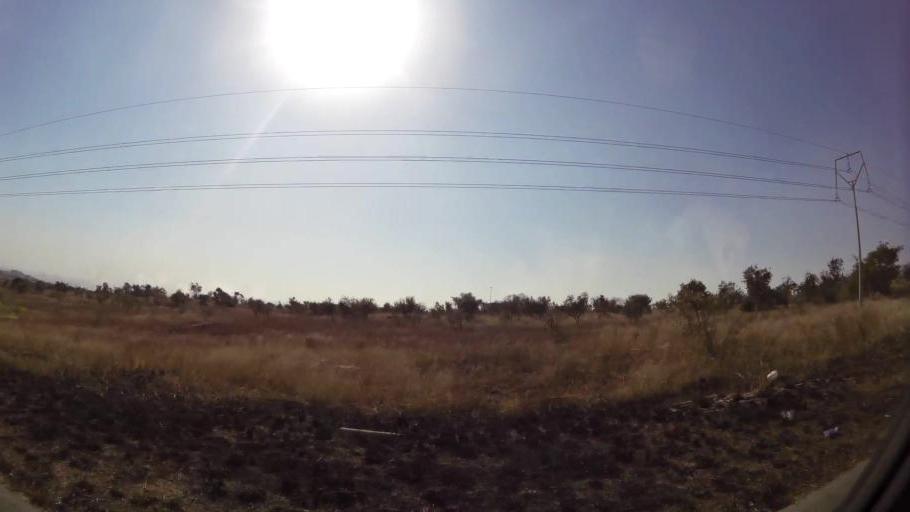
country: ZA
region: Gauteng
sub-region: City of Tshwane Metropolitan Municipality
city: Mabopane
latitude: -25.5287
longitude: 28.0927
